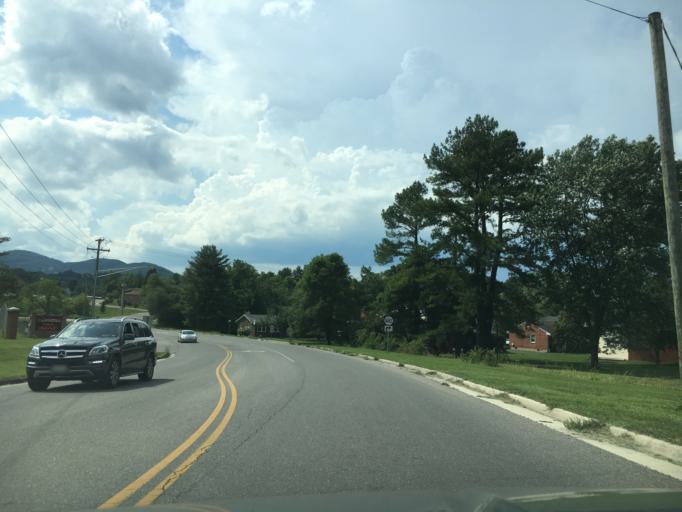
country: US
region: Virginia
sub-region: Roanoke County
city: Cave Spring
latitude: 37.2149
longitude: -80.0142
